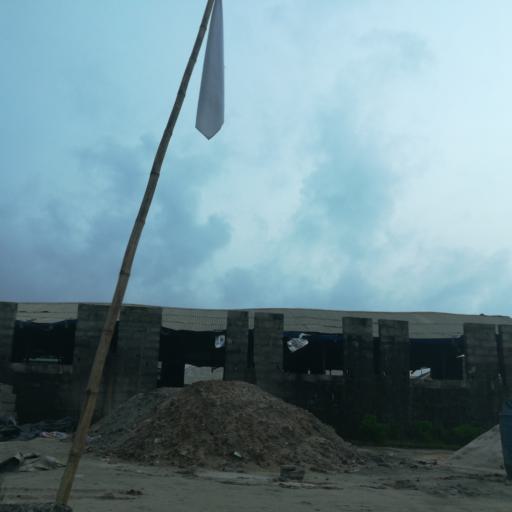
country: NG
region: Rivers
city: Port Harcourt
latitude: 4.7499
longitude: 7.0086
